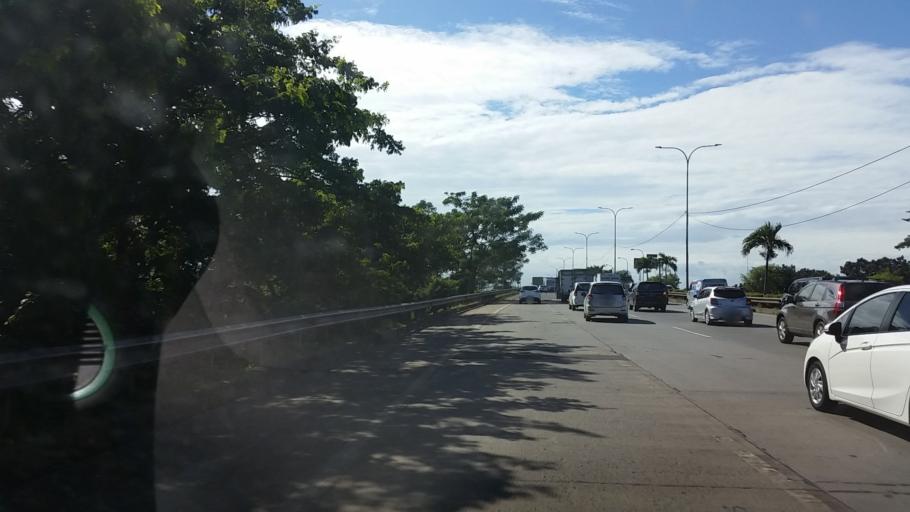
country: ID
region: Banten
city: South Tangerang
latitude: -6.2534
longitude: 106.7645
